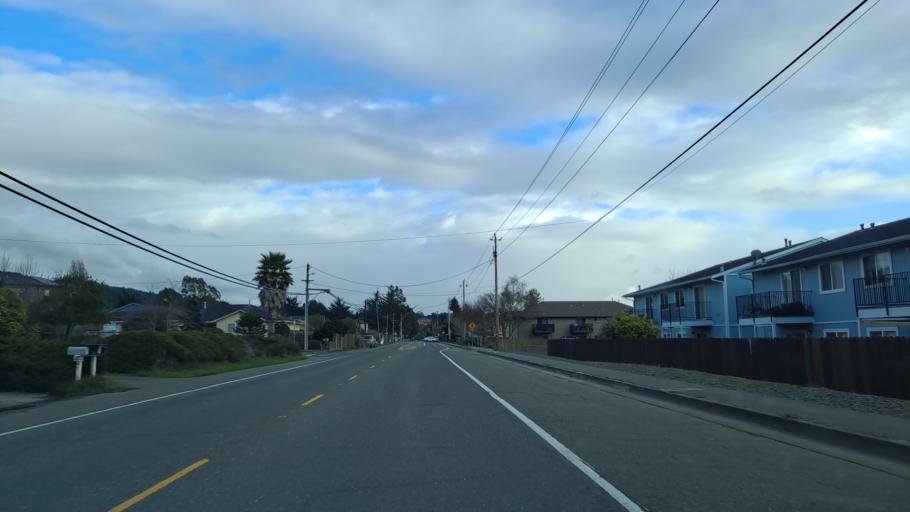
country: US
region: California
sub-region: Humboldt County
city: Fortuna
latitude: 40.5940
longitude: -124.1417
